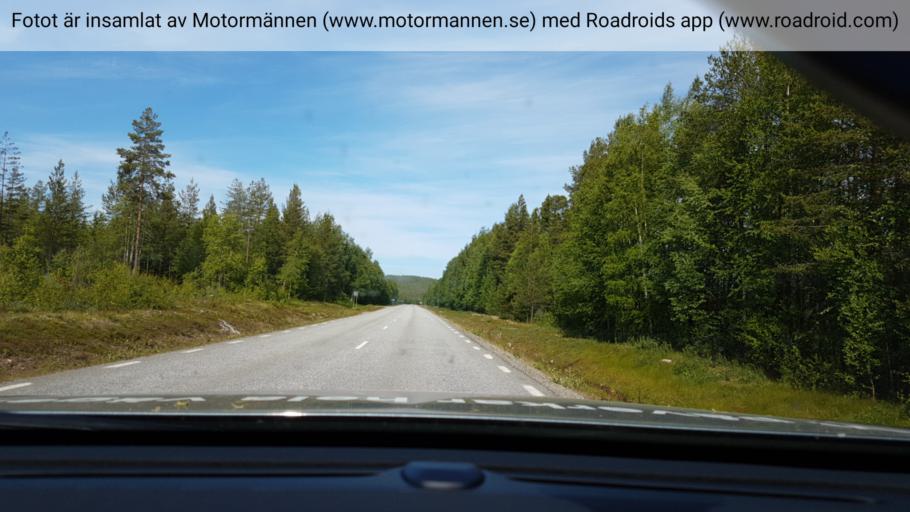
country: SE
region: Vaesterbotten
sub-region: Dorotea Kommun
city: Dorotea
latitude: 64.2262
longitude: 16.8400
